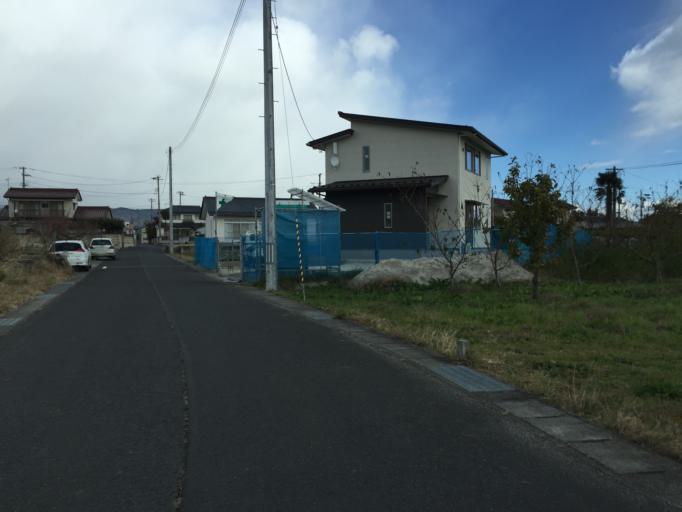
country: JP
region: Fukushima
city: Fukushima-shi
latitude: 37.8120
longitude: 140.4360
